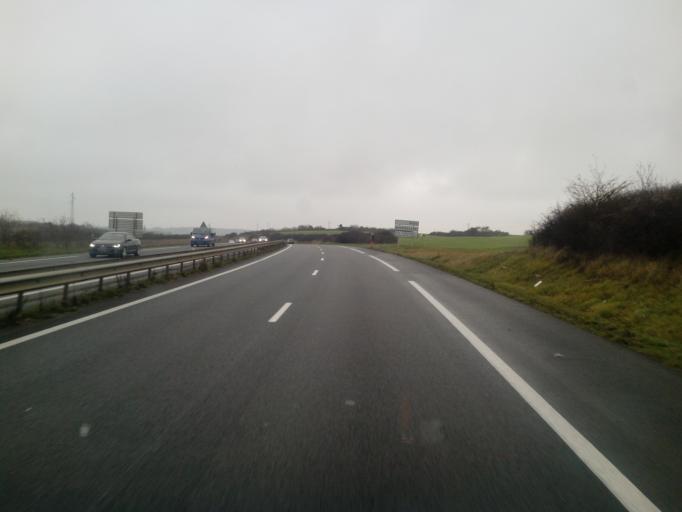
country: FR
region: Poitou-Charentes
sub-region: Departement de la Vienne
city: Chasseneuil-du-Poitou
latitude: 46.6154
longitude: 0.3838
